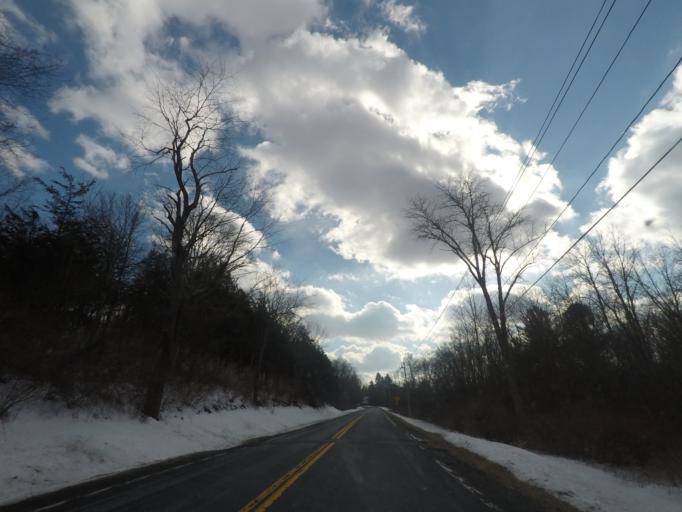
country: US
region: New York
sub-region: Schenectady County
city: Niskayuna
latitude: 42.8180
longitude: -73.8490
